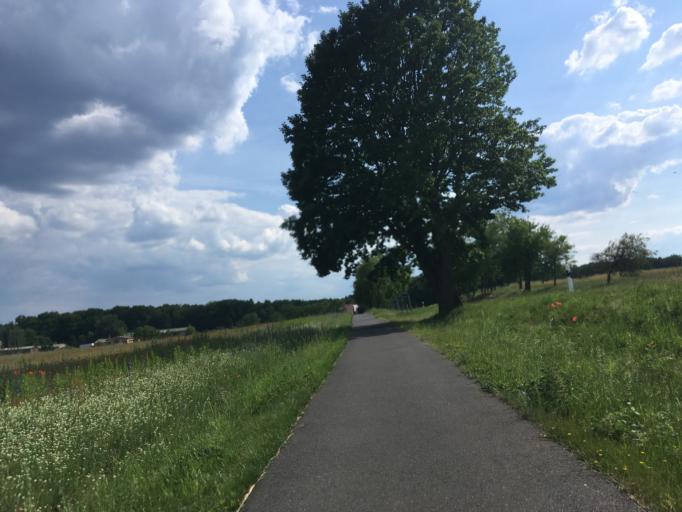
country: DE
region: Brandenburg
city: Furstenwalde
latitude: 52.4021
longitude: 14.0979
